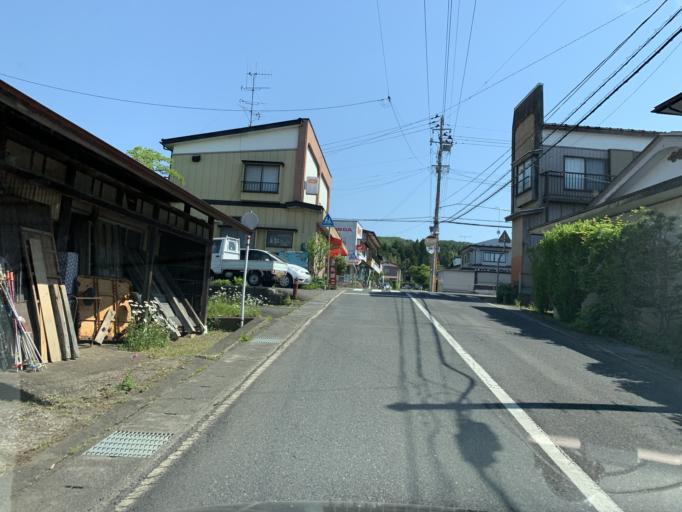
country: JP
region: Iwate
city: Mizusawa
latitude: 39.0413
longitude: 141.0640
